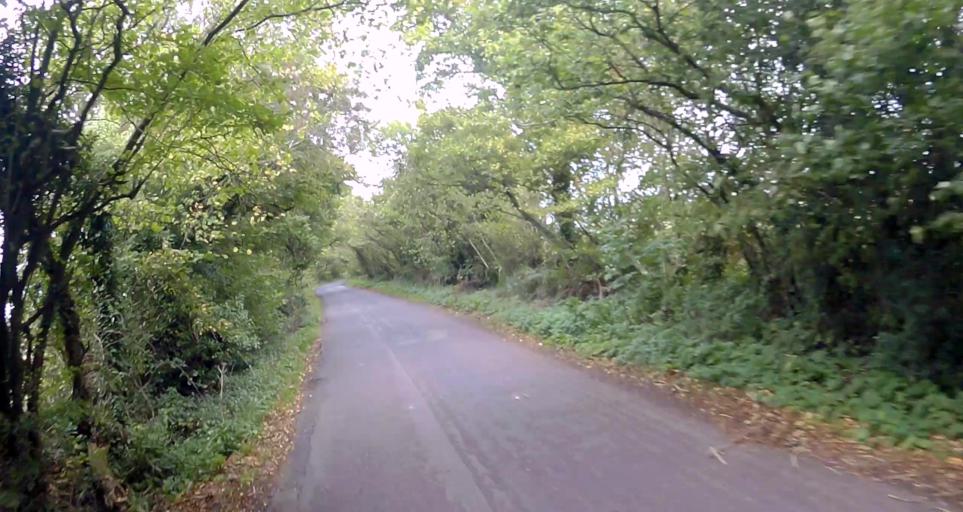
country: GB
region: England
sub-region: Hampshire
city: Four Marks
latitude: 51.1449
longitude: -1.0870
